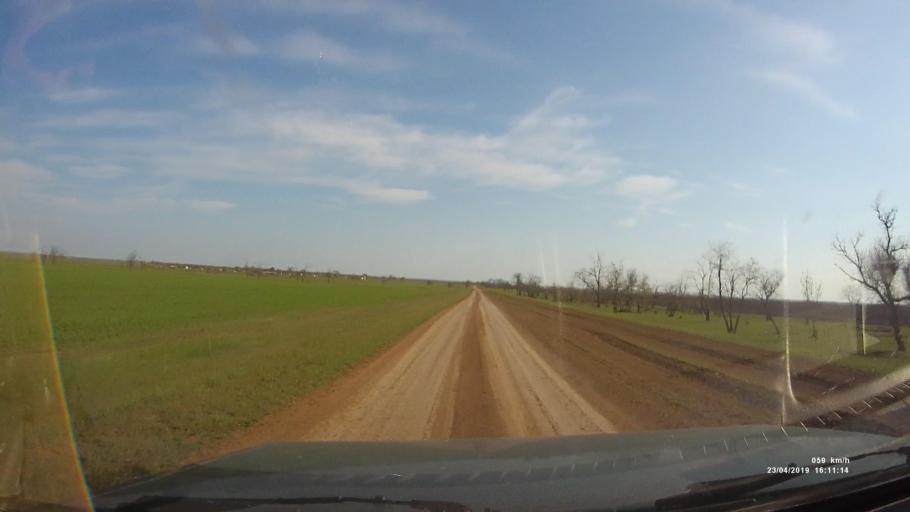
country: RU
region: Rostov
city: Remontnoye
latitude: 46.4756
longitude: 43.1231
